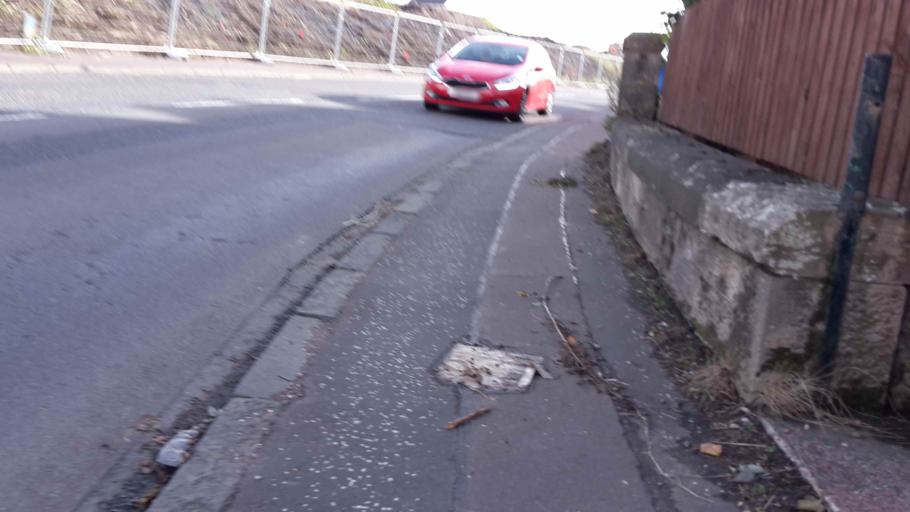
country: GB
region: Scotland
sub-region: South Lanarkshire
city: Carluke
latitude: 55.7262
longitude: -3.8325
